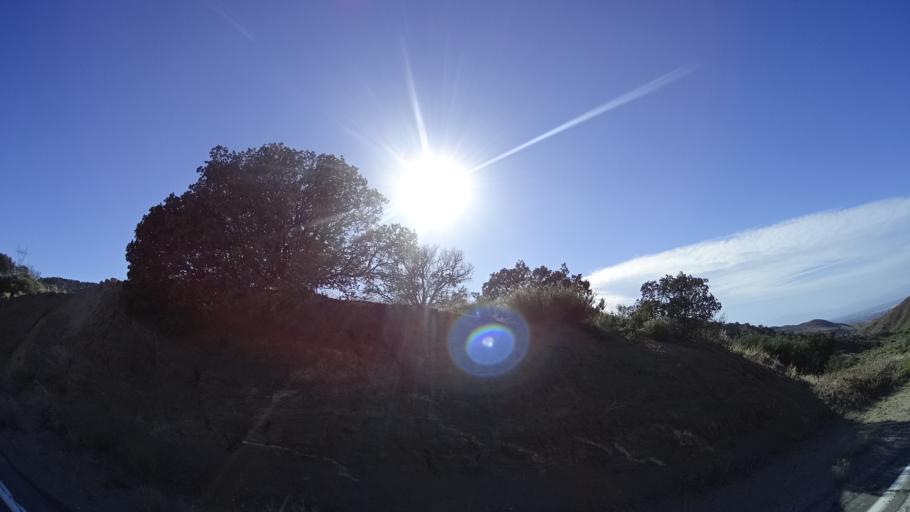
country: US
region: California
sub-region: Los Angeles County
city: Vincent
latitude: 34.4888
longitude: -118.0640
